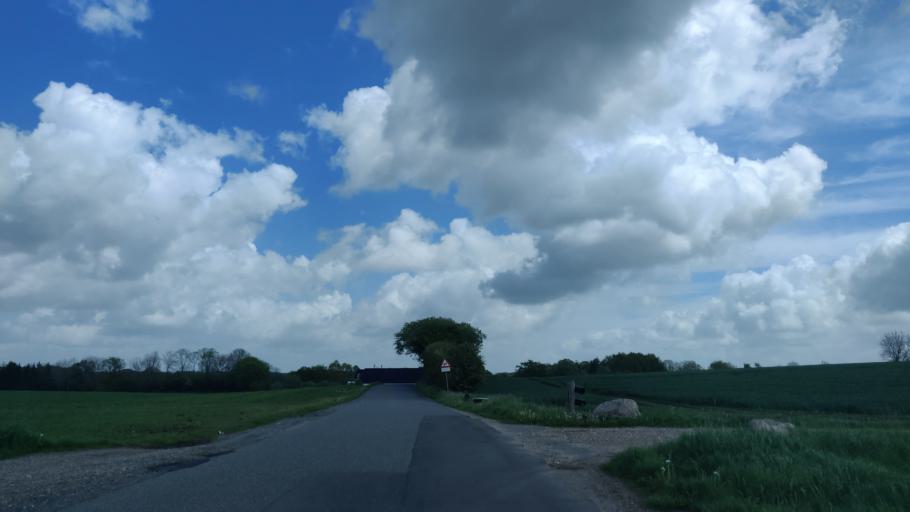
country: DK
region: South Denmark
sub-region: Vejle Kommune
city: Vejle
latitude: 55.6562
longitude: 9.5127
